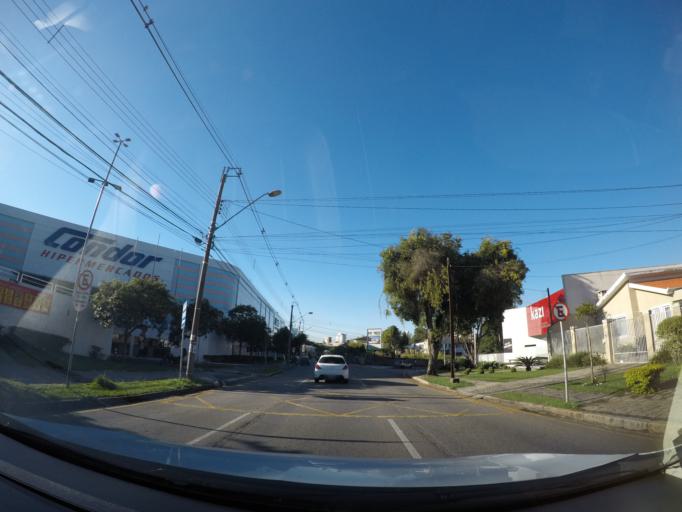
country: BR
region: Parana
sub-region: Curitiba
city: Curitiba
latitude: -25.4117
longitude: -49.2747
